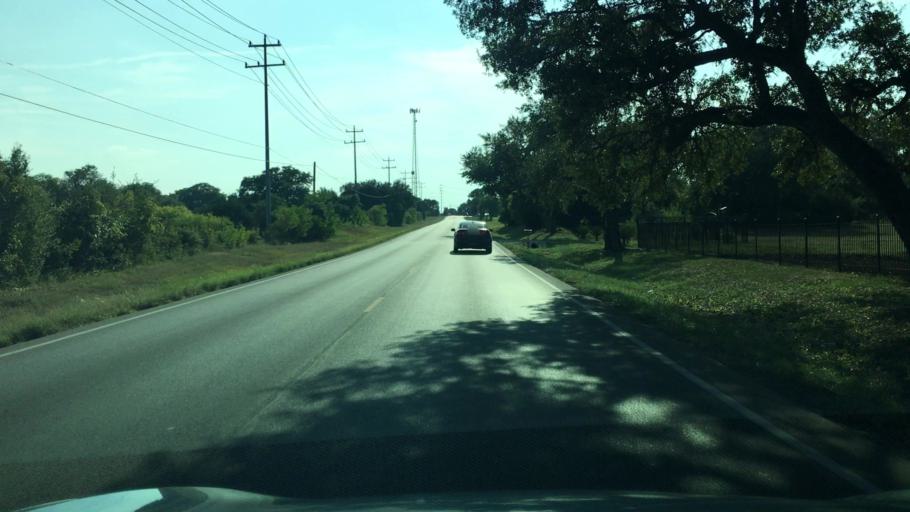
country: US
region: Texas
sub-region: Travis County
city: Shady Hollow
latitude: 30.1172
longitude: -97.9806
